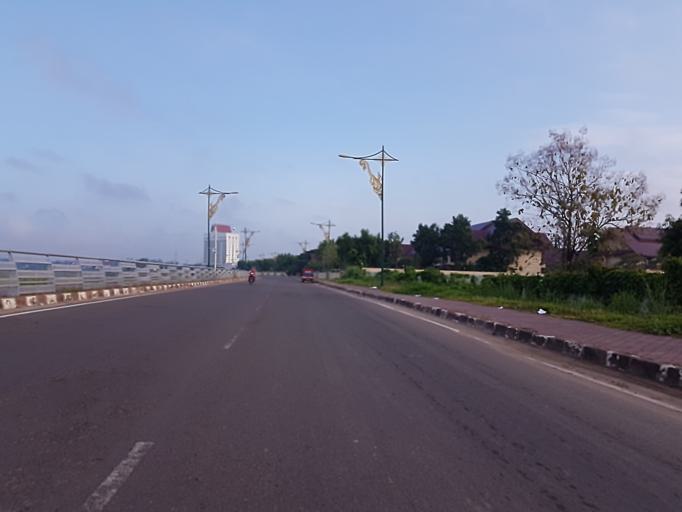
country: LA
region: Vientiane
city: Vientiane
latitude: 17.9478
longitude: 102.6158
